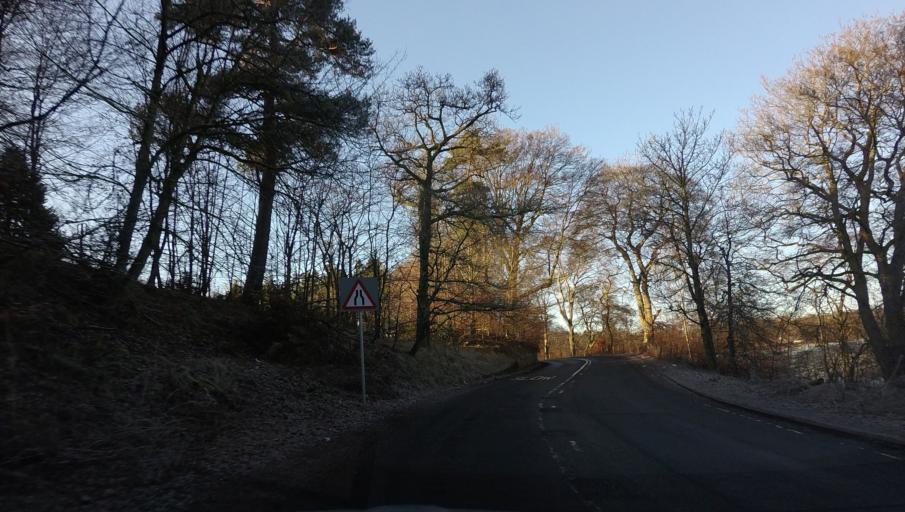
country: GB
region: Scotland
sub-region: North Lanarkshire
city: Newmains
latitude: 55.7954
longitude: -3.8529
